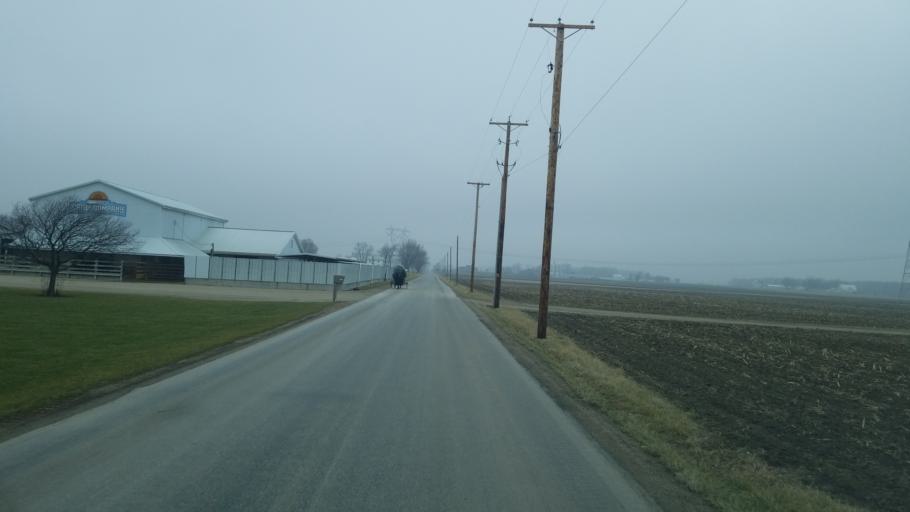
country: US
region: Indiana
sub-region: Adams County
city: Berne
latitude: 40.7055
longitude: -84.9753
